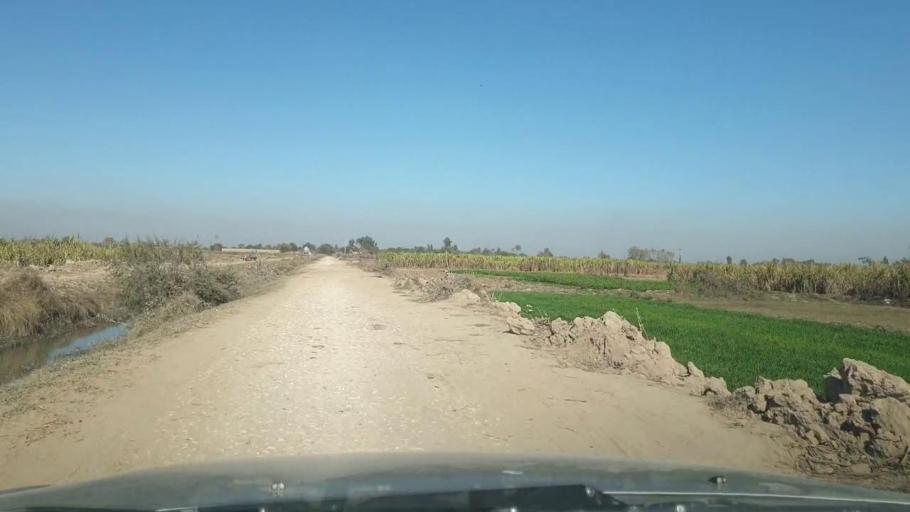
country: PK
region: Sindh
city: Ghotki
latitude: 28.0369
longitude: 69.2465
